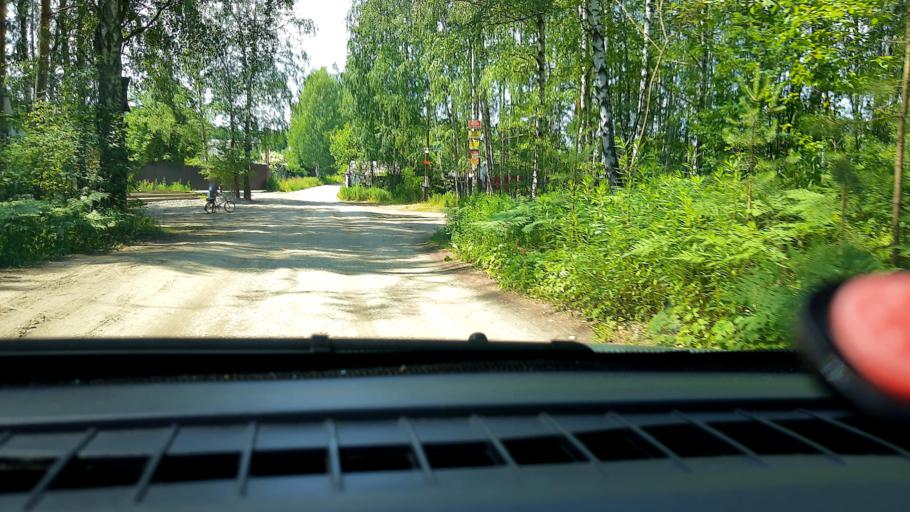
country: RU
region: Nizjnij Novgorod
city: Neklyudovo
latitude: 56.4503
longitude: 43.9973
